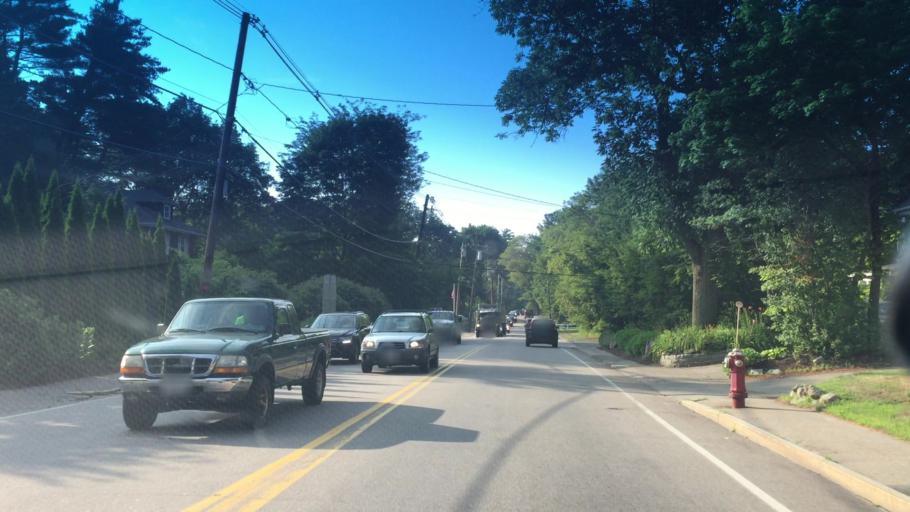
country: US
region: Massachusetts
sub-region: Norfolk County
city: Medfield
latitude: 42.1847
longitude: -71.3081
